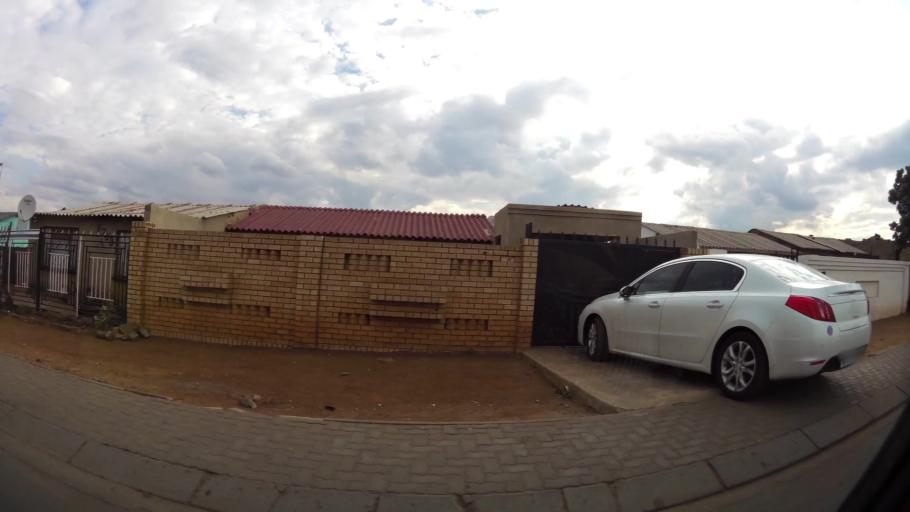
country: ZA
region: Gauteng
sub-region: City of Johannesburg Metropolitan Municipality
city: Soweto
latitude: -26.2483
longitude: 27.8183
